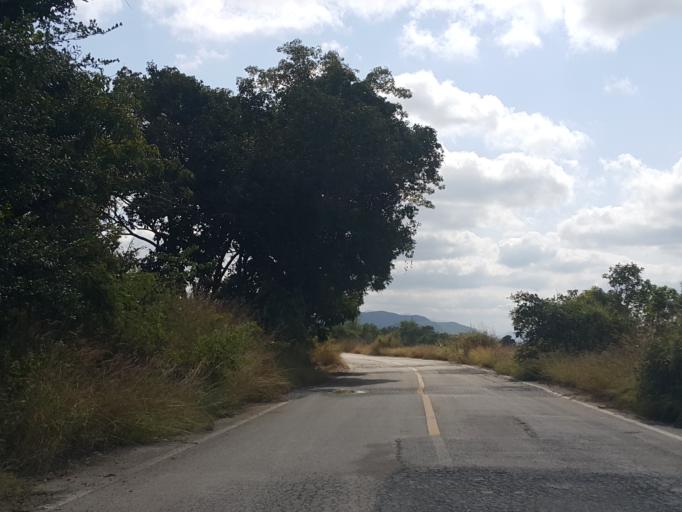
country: TH
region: Lamphun
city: Lamphun
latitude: 18.5533
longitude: 99.0864
